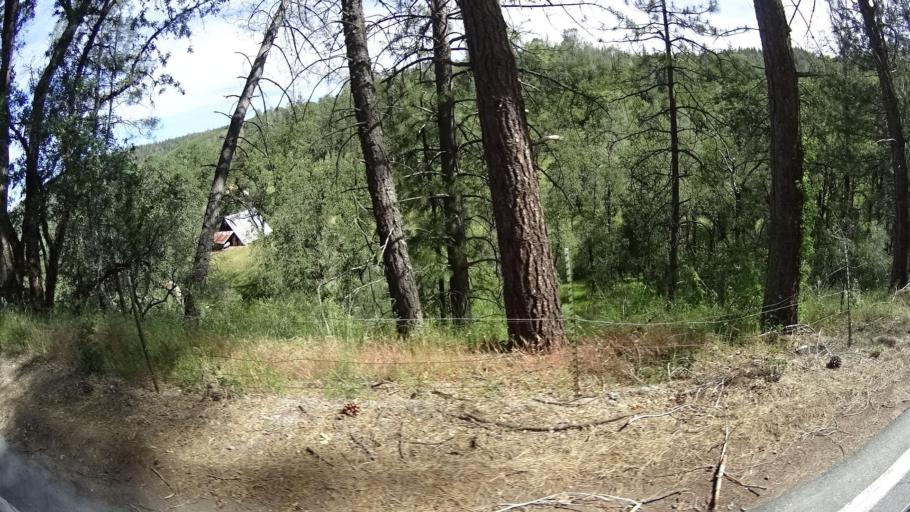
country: US
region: California
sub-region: Lake County
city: Cobb
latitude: 38.8585
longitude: -122.7439
